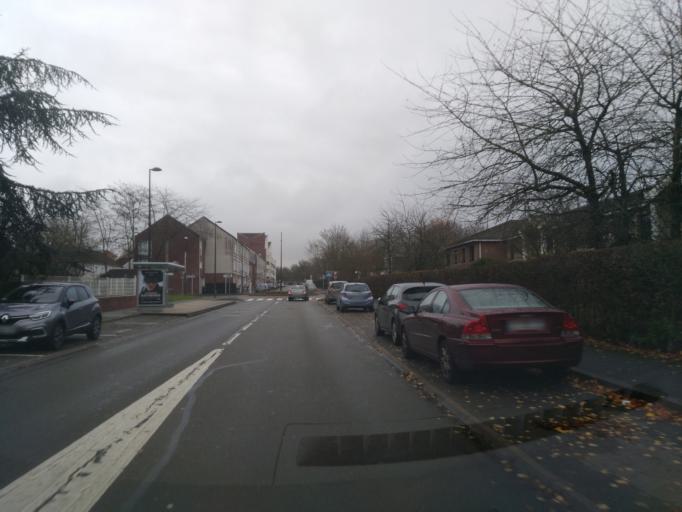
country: FR
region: Ile-de-France
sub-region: Departement des Yvelines
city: Voisins-le-Bretonneux
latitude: 48.7652
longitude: 2.0594
